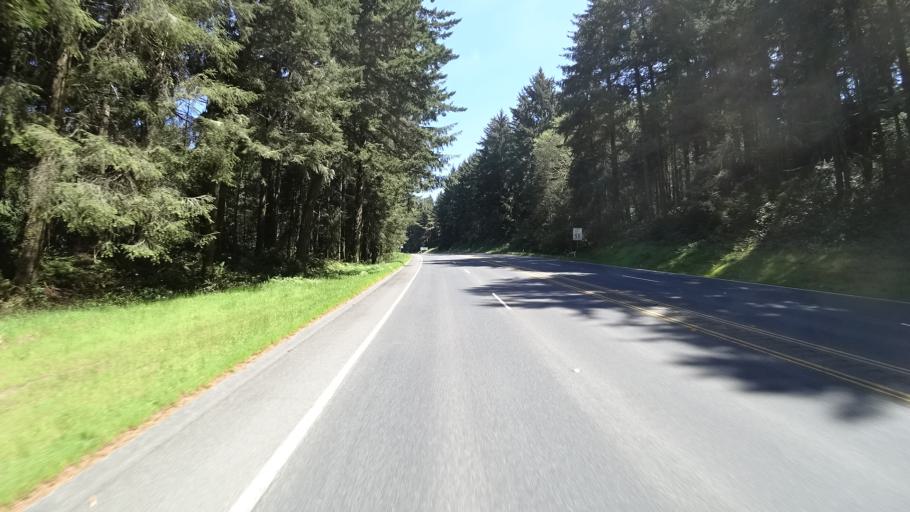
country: US
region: California
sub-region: Humboldt County
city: Westhaven-Moonstone
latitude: 41.1392
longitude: -124.1392
